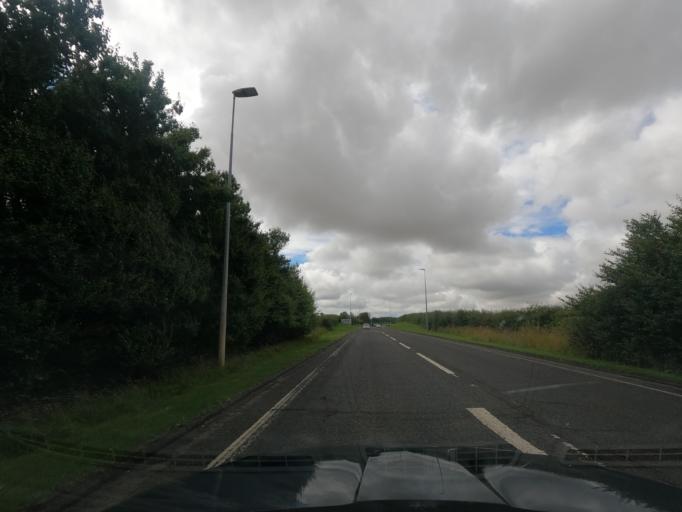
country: GB
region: England
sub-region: Northumberland
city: Ancroft
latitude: 55.7400
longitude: -1.9974
